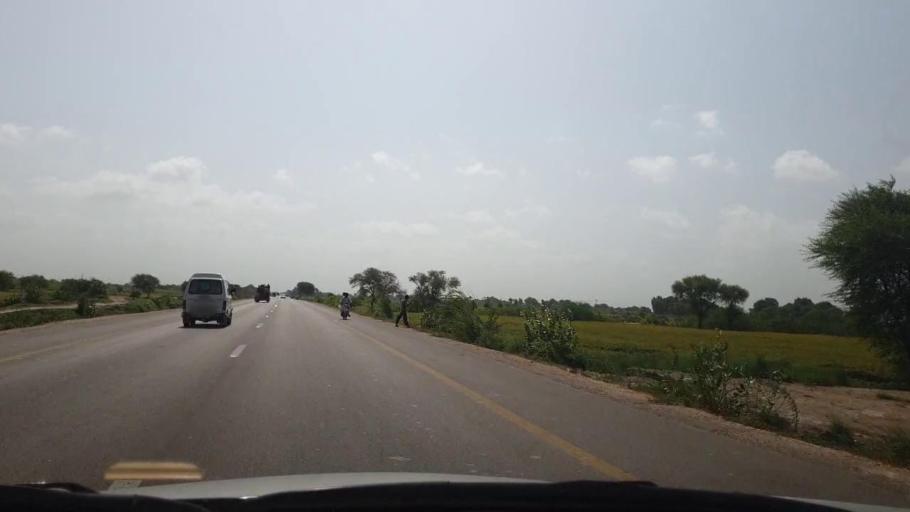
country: PK
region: Sindh
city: Matli
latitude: 24.9823
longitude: 68.6645
